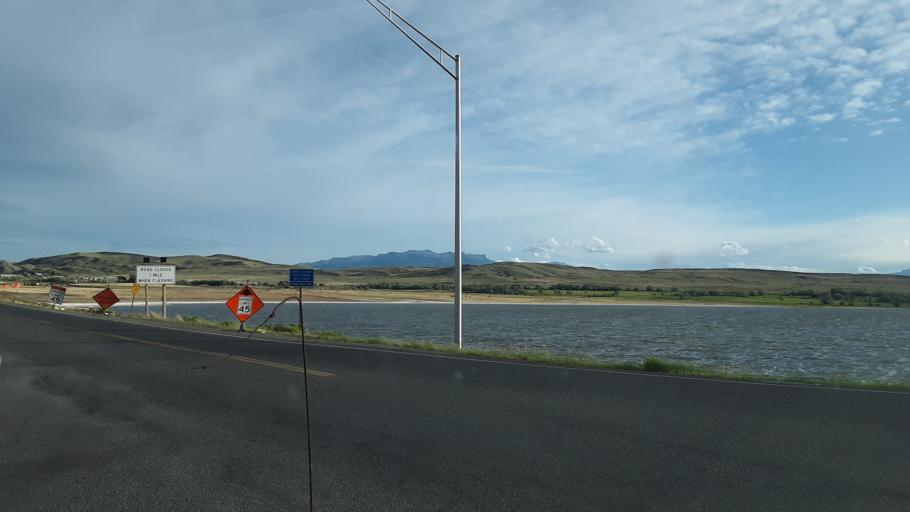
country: US
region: Wyoming
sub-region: Park County
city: Cody
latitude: 44.5115
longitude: -109.0260
